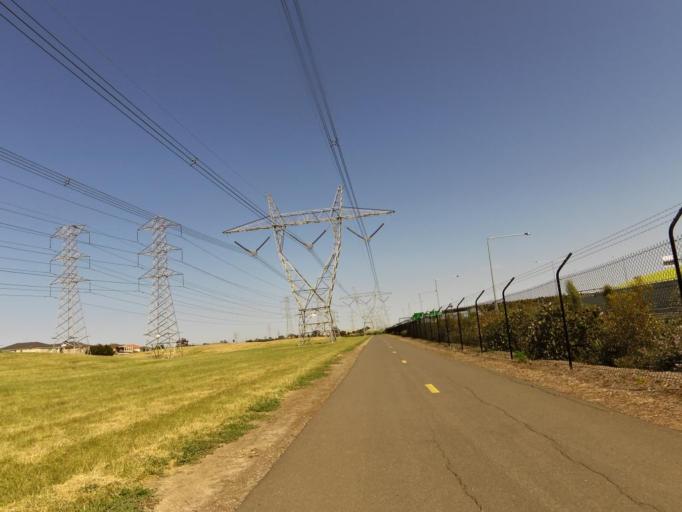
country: AU
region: Victoria
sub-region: Moreland
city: Gowanbrae
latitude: -37.7010
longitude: 144.8950
